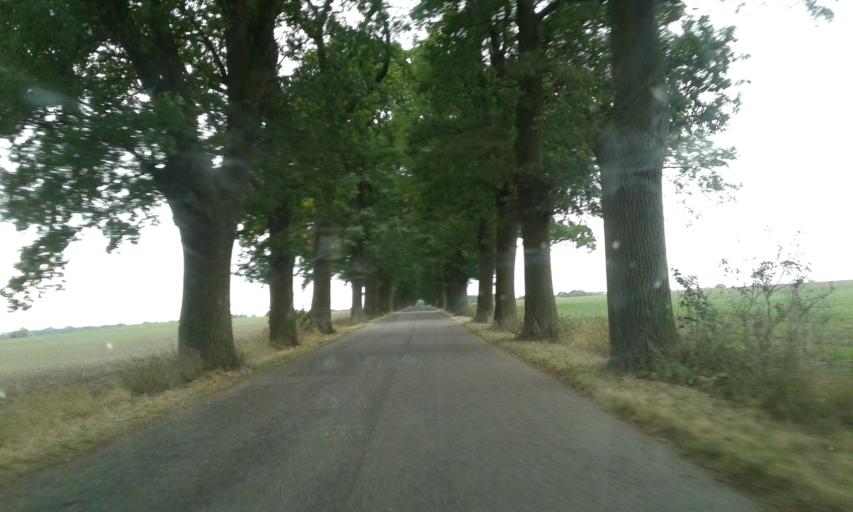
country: PL
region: West Pomeranian Voivodeship
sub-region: Powiat pyrzycki
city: Przelewice
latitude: 53.1802
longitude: 15.0417
